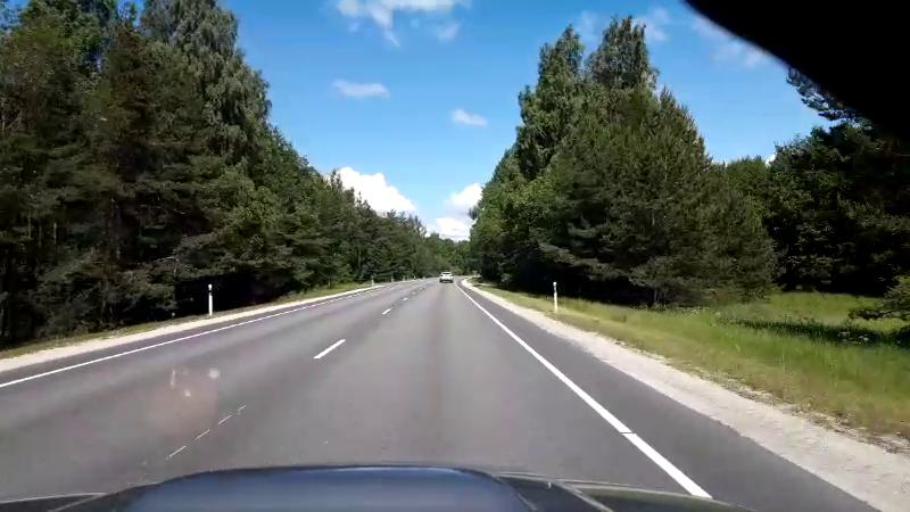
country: EE
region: Paernumaa
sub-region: Paernu linn
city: Parnu
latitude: 58.2166
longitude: 24.4873
